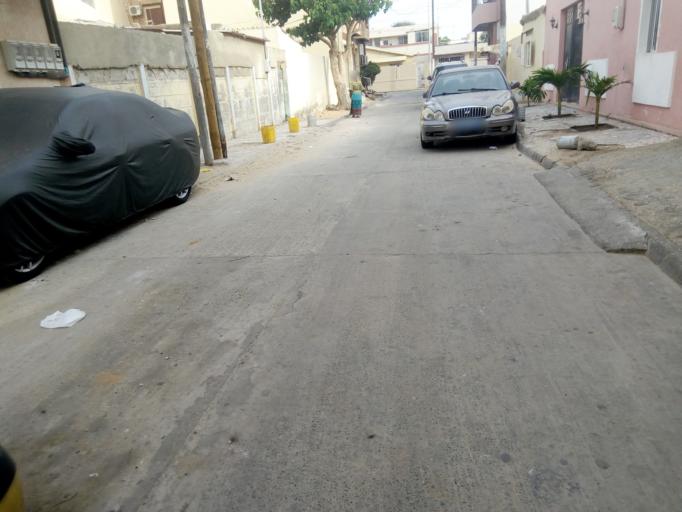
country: SN
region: Dakar
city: Dakar
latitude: 14.7001
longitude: -17.4552
